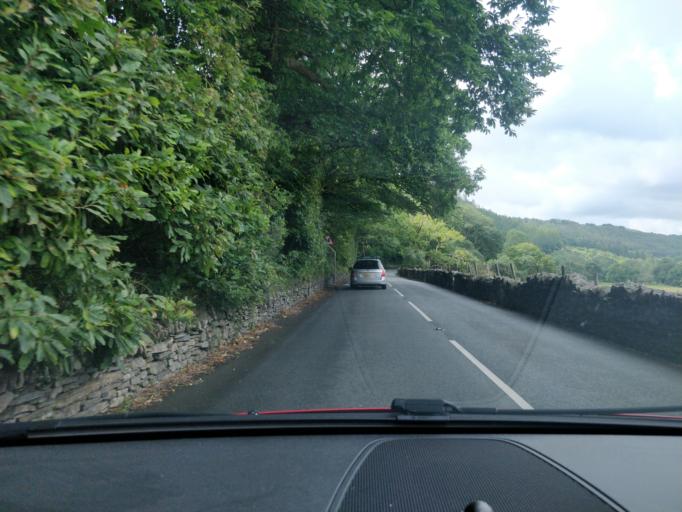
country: GB
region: Wales
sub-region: Gwynedd
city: Ffestiniog
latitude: 52.9590
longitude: -3.9530
